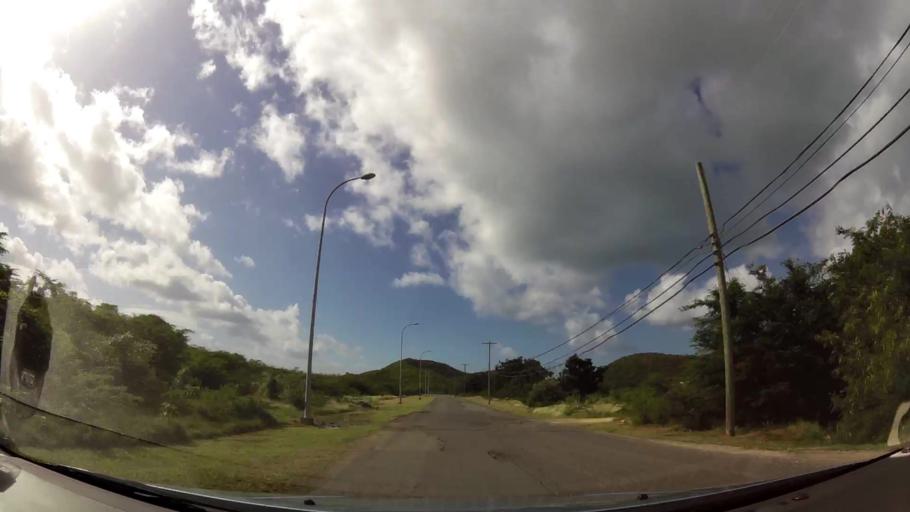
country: AG
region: Saint John
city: Saint John's
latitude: 17.1173
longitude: -61.8643
